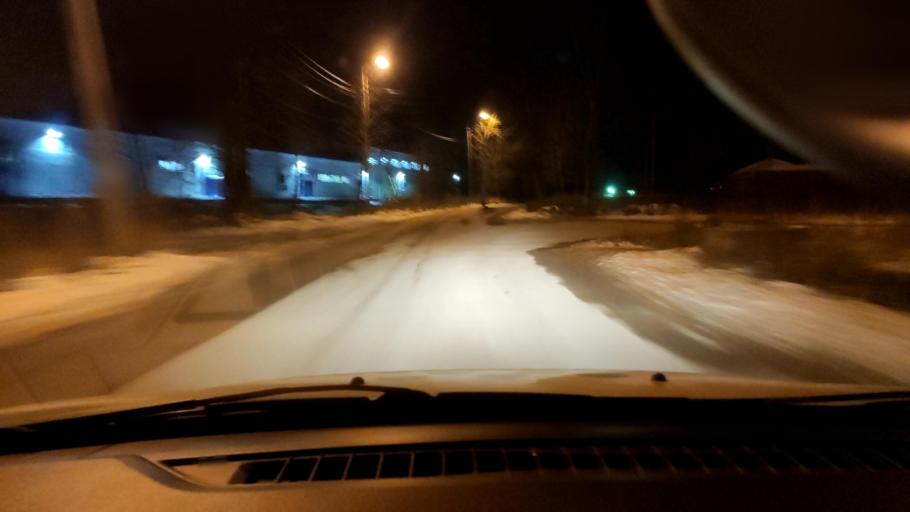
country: RU
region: Perm
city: Overyata
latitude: 58.0108
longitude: 55.9407
